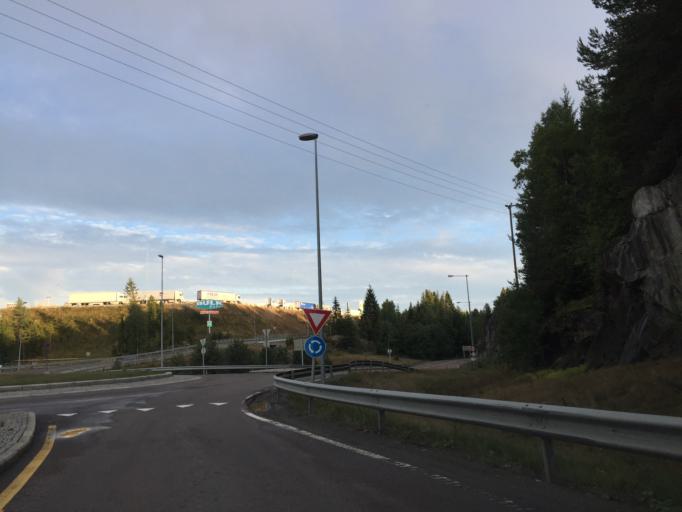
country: NO
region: Akershus
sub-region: Ski
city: Ski
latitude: 59.7756
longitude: 10.8502
